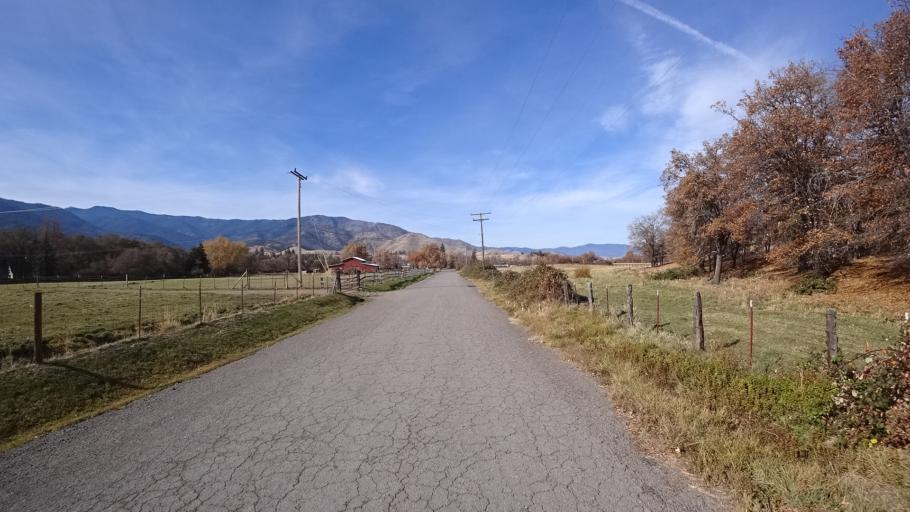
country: US
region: California
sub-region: Siskiyou County
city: Weed
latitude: 41.4468
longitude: -122.4277
